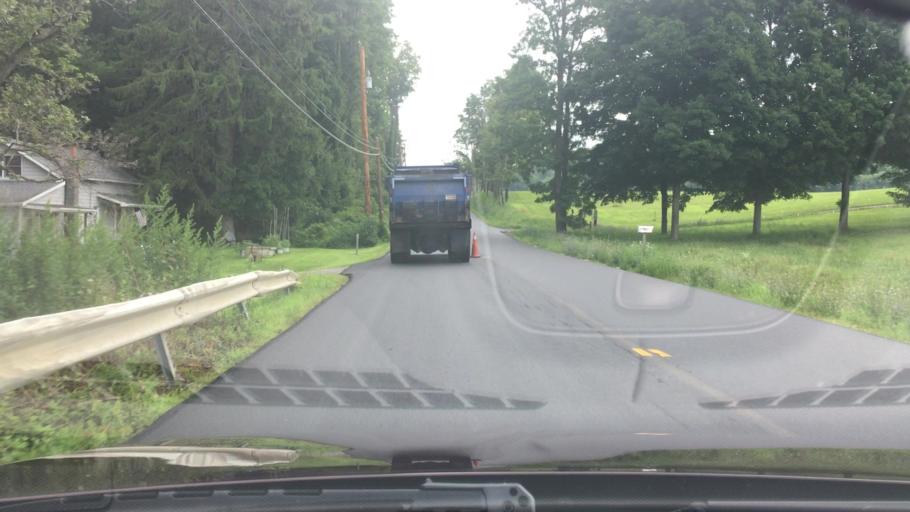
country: US
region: New York
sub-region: Dutchess County
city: Hillside Lake
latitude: 41.5805
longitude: -73.7322
